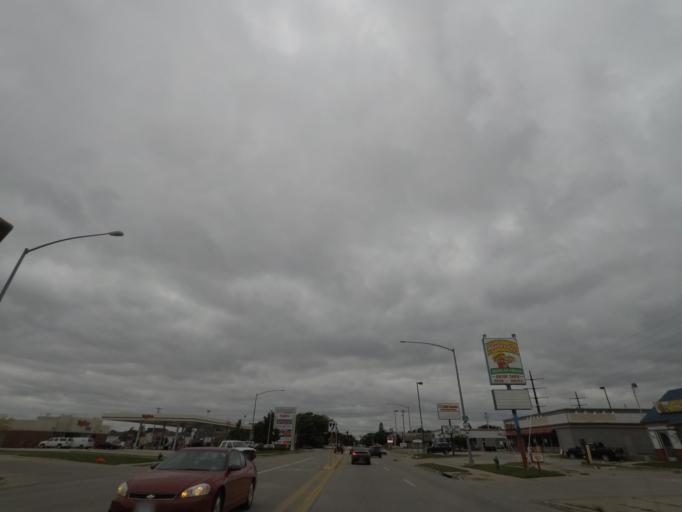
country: US
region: Iowa
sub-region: Story County
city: Ames
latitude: 42.0230
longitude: -93.6181
